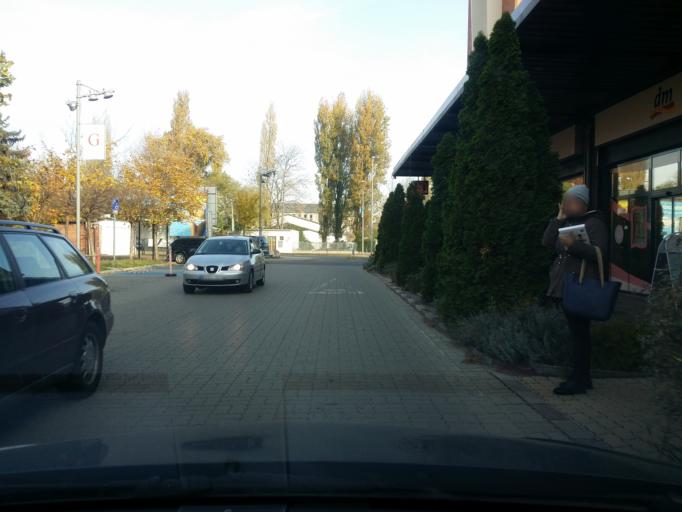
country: HU
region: Budapest
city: Budapest XI. keruelet
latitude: 47.4606
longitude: 19.0511
